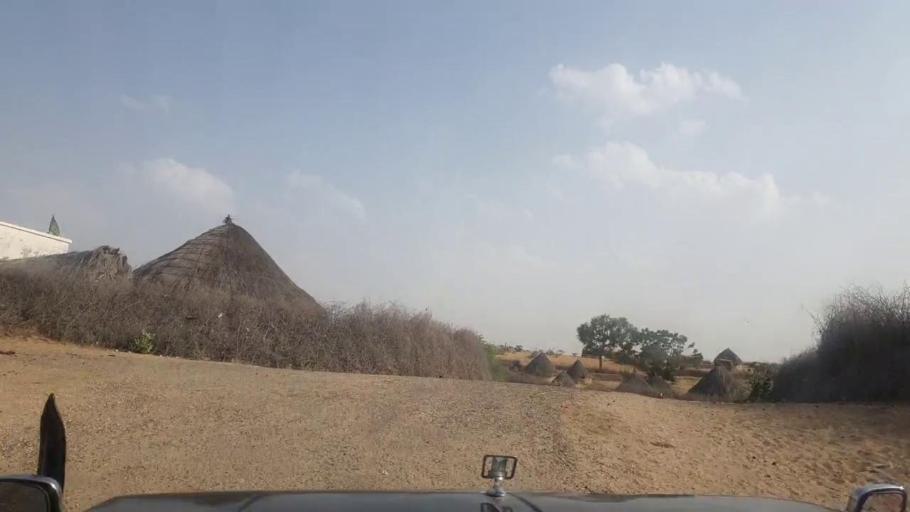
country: PK
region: Sindh
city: Islamkot
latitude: 25.1334
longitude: 70.3247
